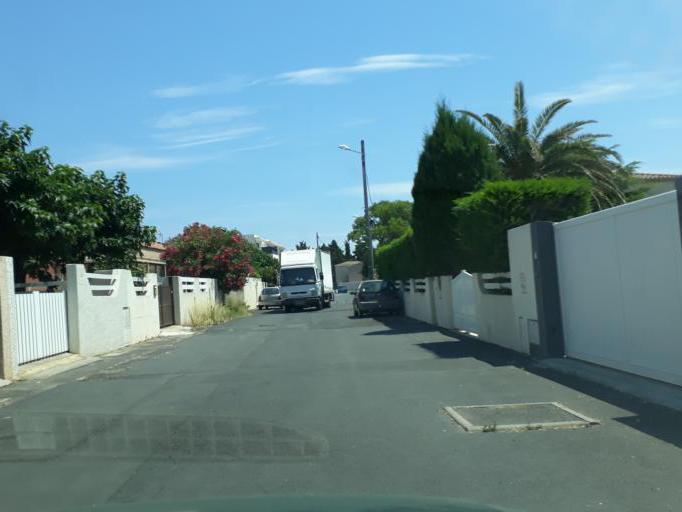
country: FR
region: Languedoc-Roussillon
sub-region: Departement de l'Herault
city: Agde
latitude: 43.2899
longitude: 3.4510
